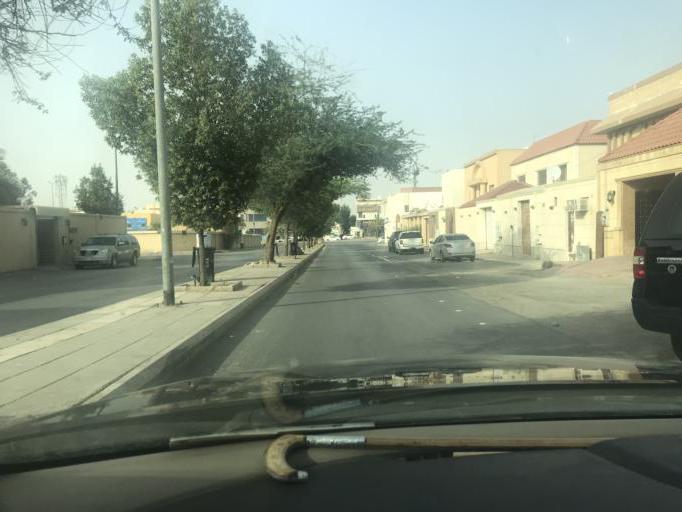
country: SA
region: Ar Riyad
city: Riyadh
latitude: 24.7245
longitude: 46.7690
